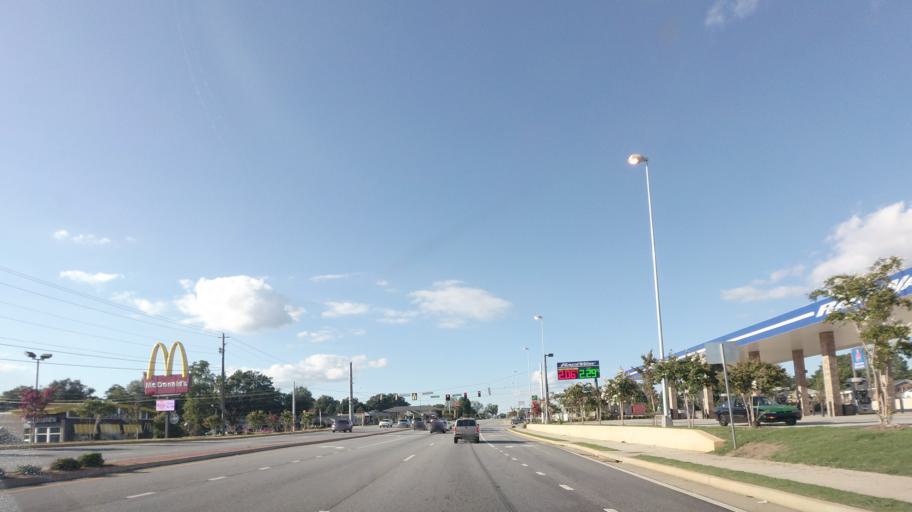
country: US
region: Georgia
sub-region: Upson County
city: Hannahs Mill
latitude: 32.9258
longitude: -84.3338
